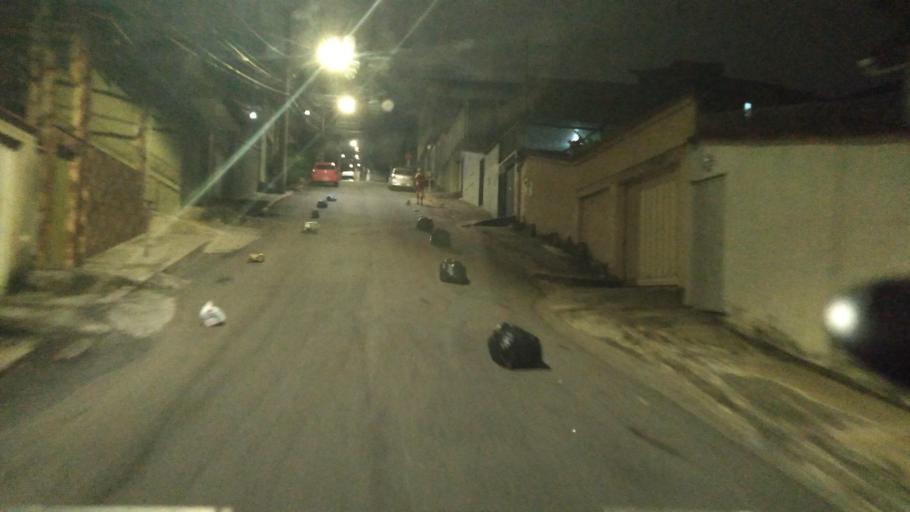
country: BR
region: Minas Gerais
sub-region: Belo Horizonte
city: Belo Horizonte
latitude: -19.8872
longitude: -43.9586
